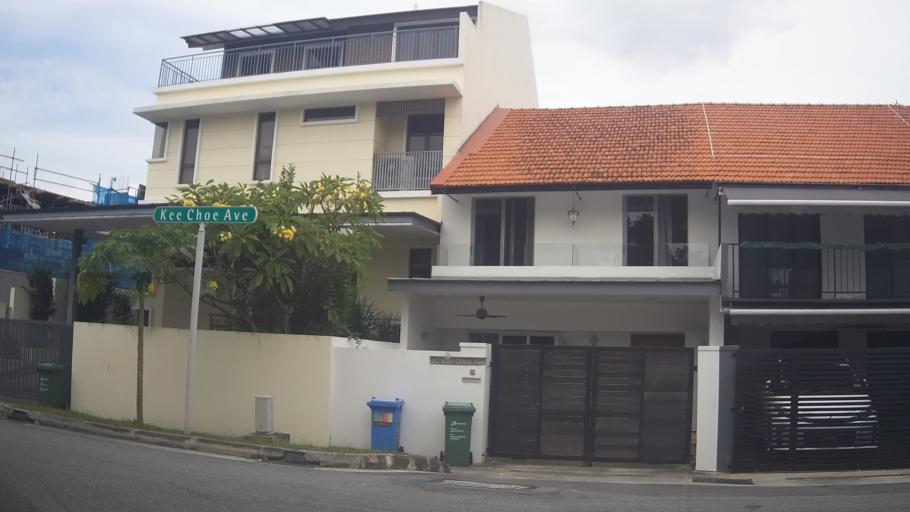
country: SG
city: Singapore
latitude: 1.3307
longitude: 103.8732
